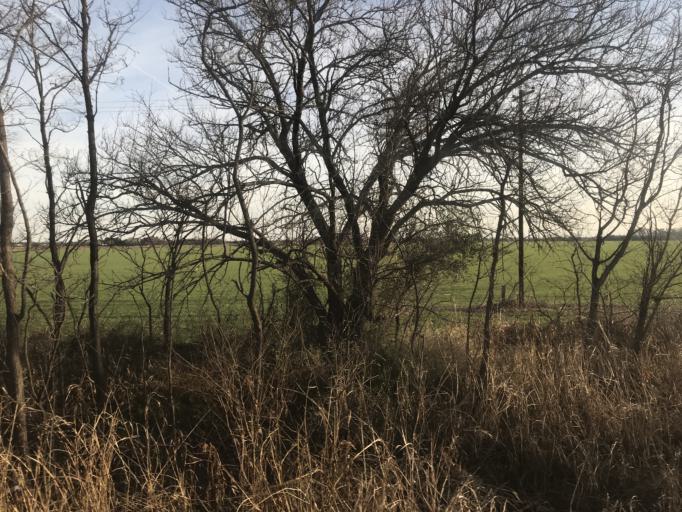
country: AR
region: Cordoba
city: Malvinas Argentinas
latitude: -31.4713
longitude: -64.0967
